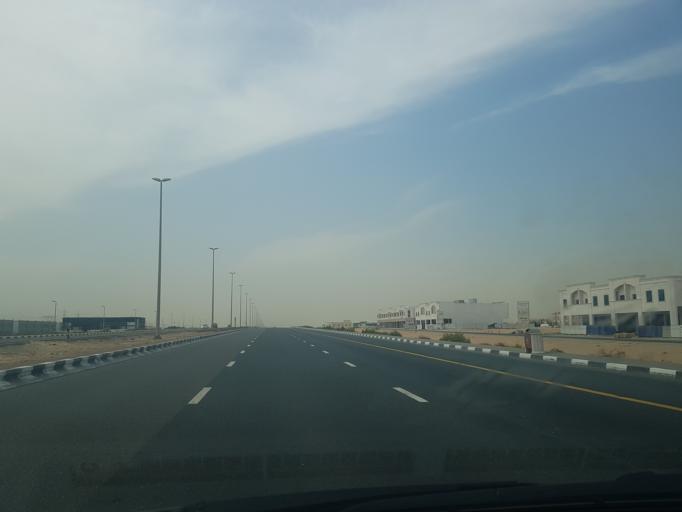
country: AE
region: Ash Shariqah
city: Sharjah
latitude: 25.2509
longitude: 55.5335
